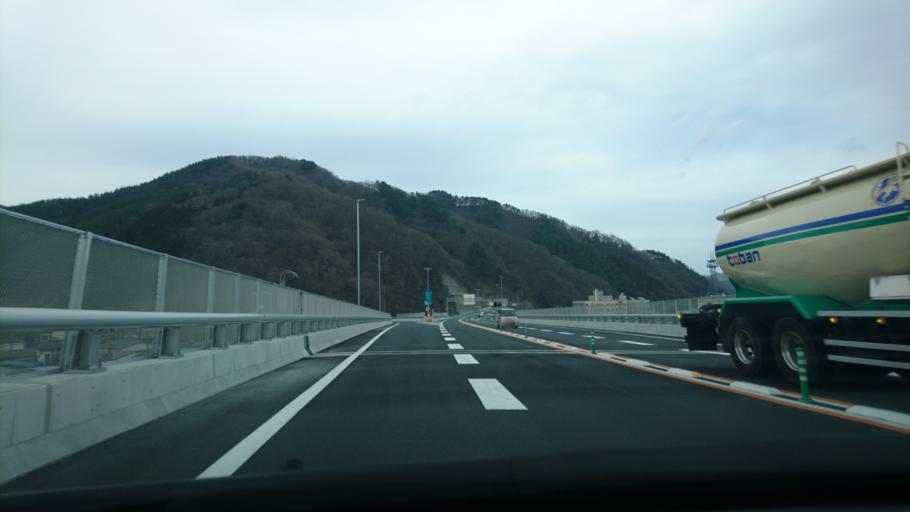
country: JP
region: Iwate
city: Kamaishi
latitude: 39.2634
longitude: 141.8414
